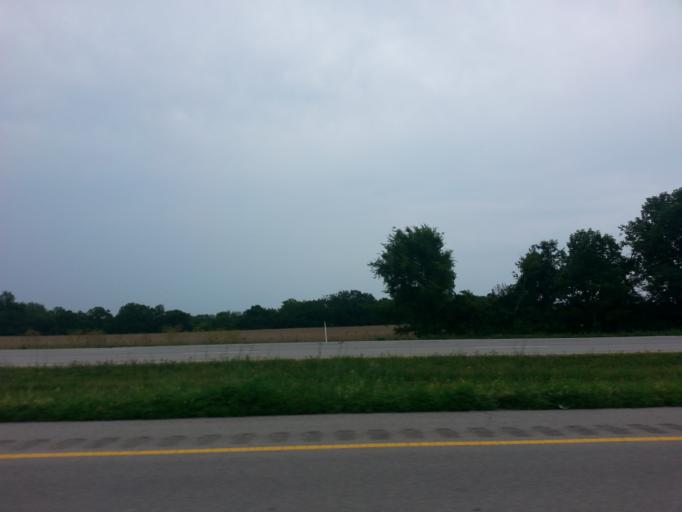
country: US
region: Ohio
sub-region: Brown County
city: Ripley
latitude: 38.8007
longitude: -83.7955
